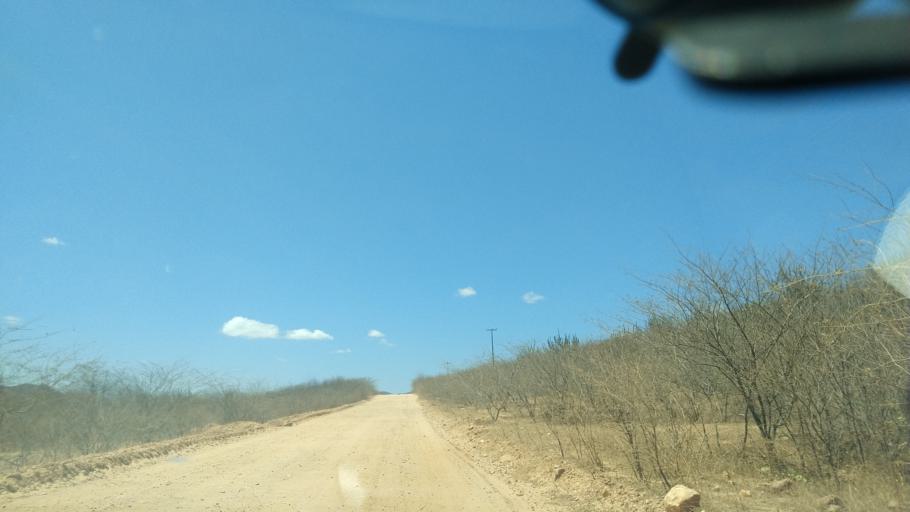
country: BR
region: Rio Grande do Norte
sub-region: Sao Tome
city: Sao Tome
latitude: -5.9714
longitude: -36.1634
